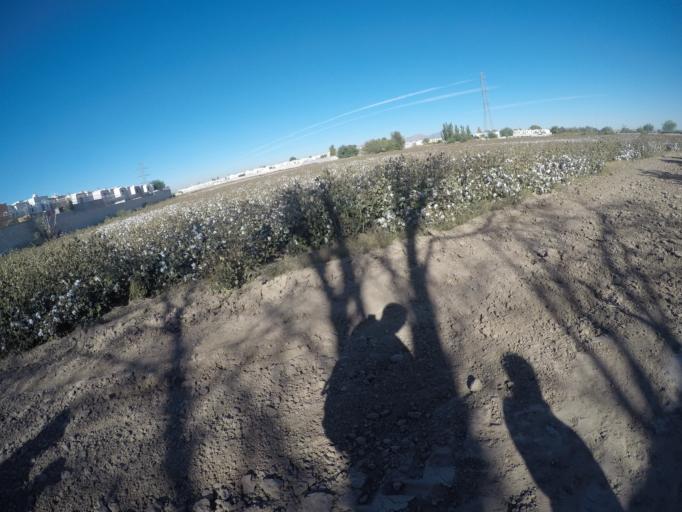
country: US
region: Texas
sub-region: El Paso County
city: Socorro
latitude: 31.6981
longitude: -106.3755
